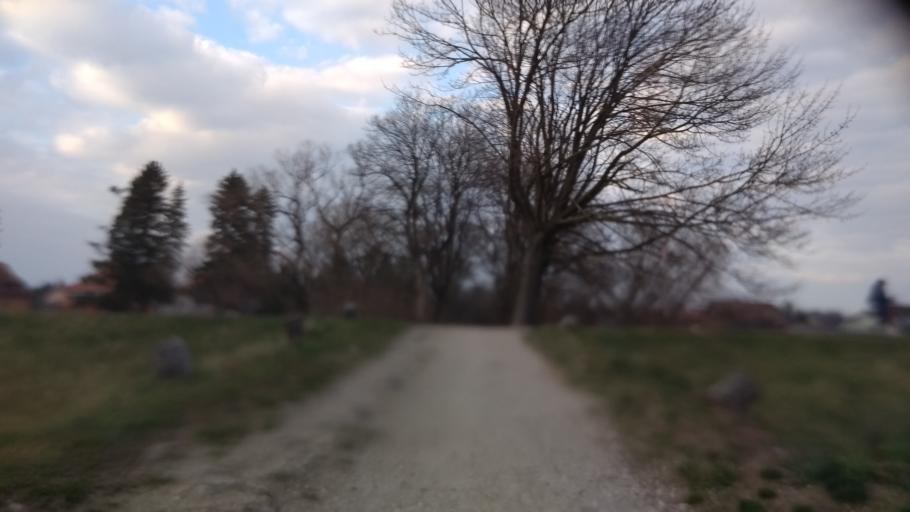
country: PL
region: Lower Silesian Voivodeship
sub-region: Jelenia Gora
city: Cieplice Slaskie Zdroj
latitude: 50.8572
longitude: 15.6721
